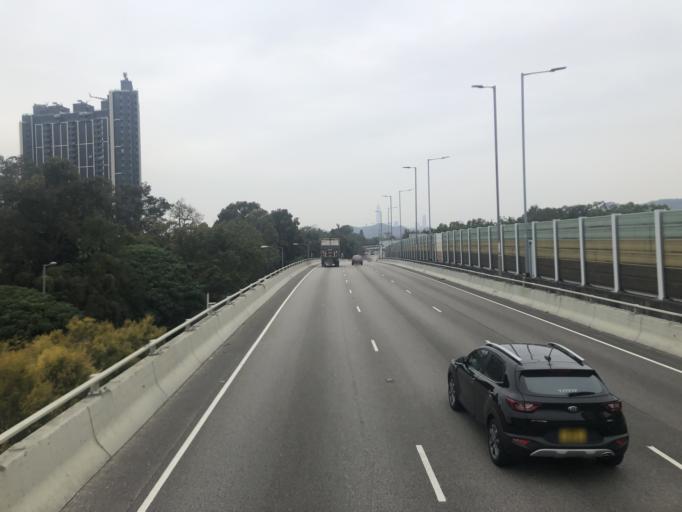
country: HK
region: Tai Po
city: Tai Po
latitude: 22.5000
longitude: 114.1239
